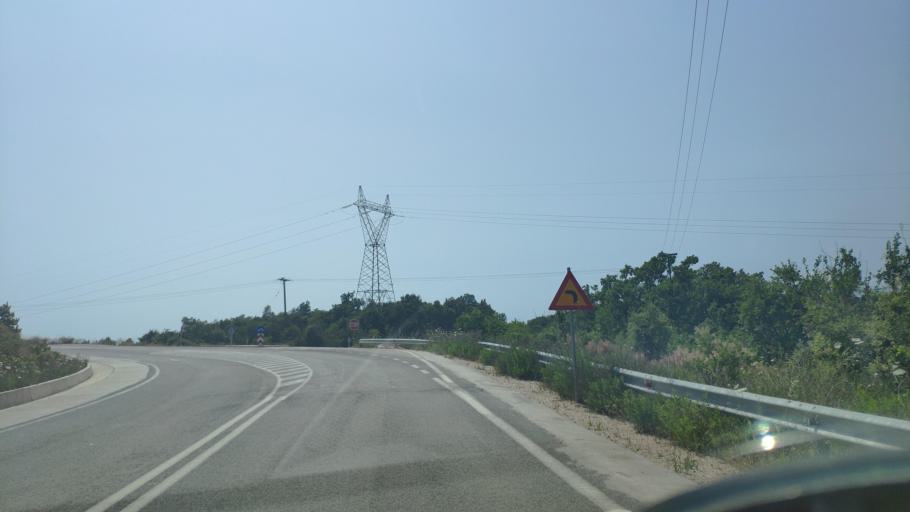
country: GR
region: Epirus
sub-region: Nomos Artas
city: Peta
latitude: 39.1975
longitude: 21.1075
